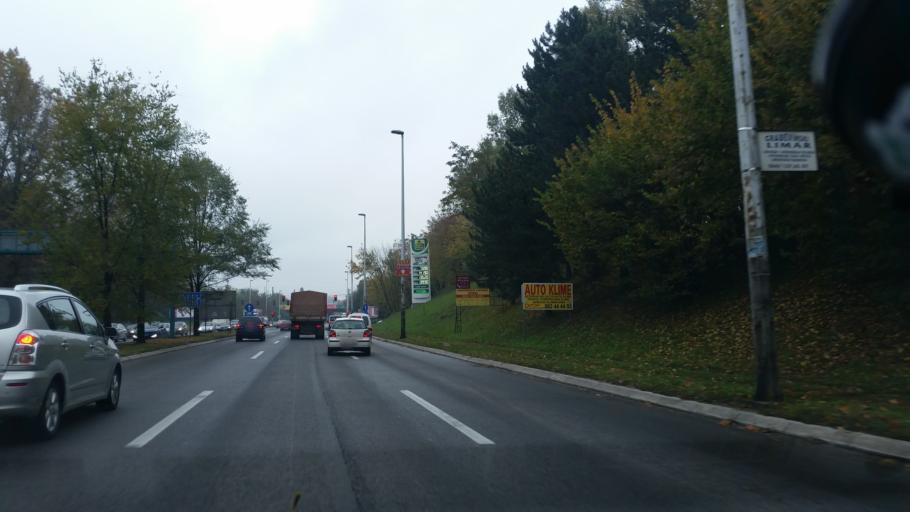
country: RS
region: Central Serbia
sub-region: Belgrade
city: Zemun
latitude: 44.8353
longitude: 20.3644
